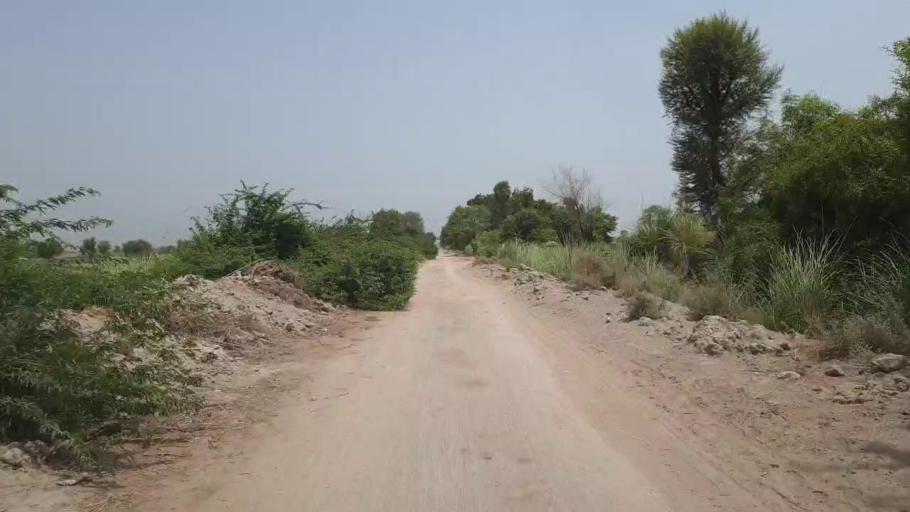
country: PK
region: Sindh
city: Nawabshah
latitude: 26.3119
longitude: 68.3010
